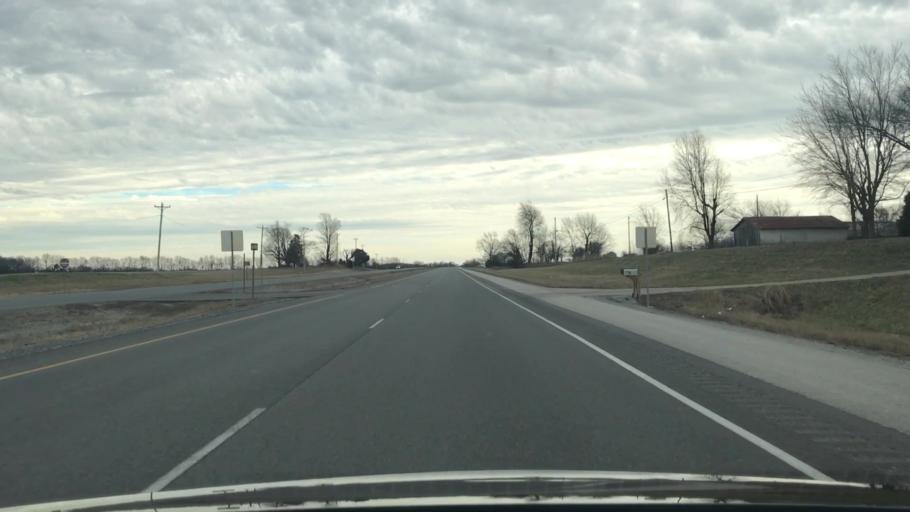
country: US
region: Kentucky
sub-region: Trigg County
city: Cadiz
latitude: 36.8819
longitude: -87.6935
